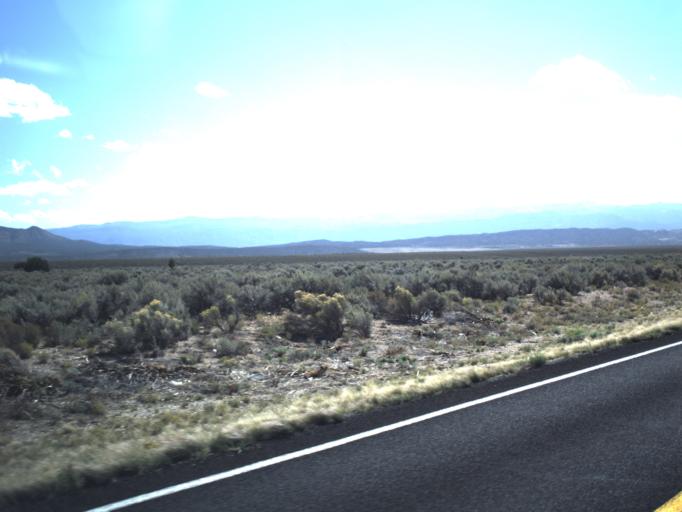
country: US
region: Utah
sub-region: Iron County
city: Enoch
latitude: 38.0070
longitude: -112.9979
